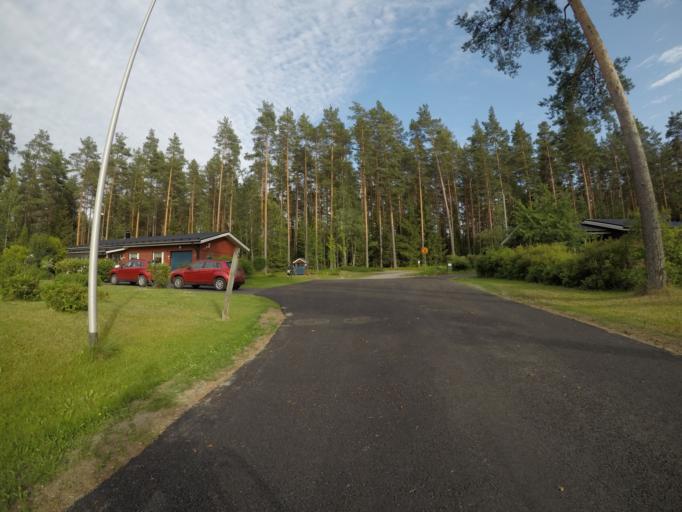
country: FI
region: Haeme
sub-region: Haemeenlinna
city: Haemeenlinna
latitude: 60.9718
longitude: 24.3967
